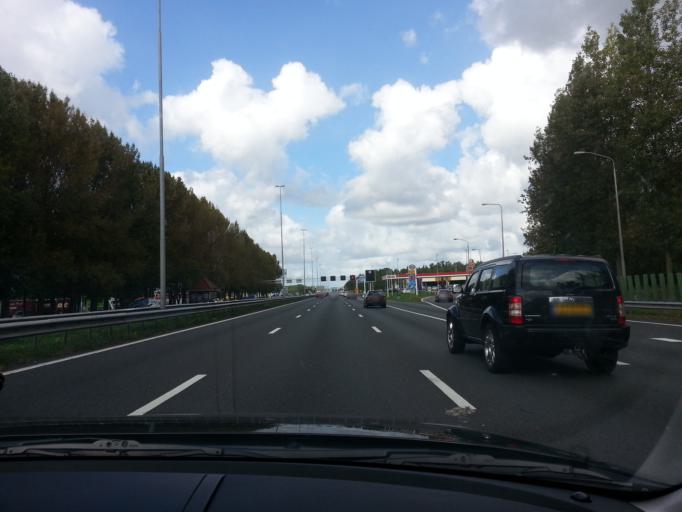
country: NL
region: South Holland
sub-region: Gemeente Delft
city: Delft
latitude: 51.9814
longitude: 4.3955
